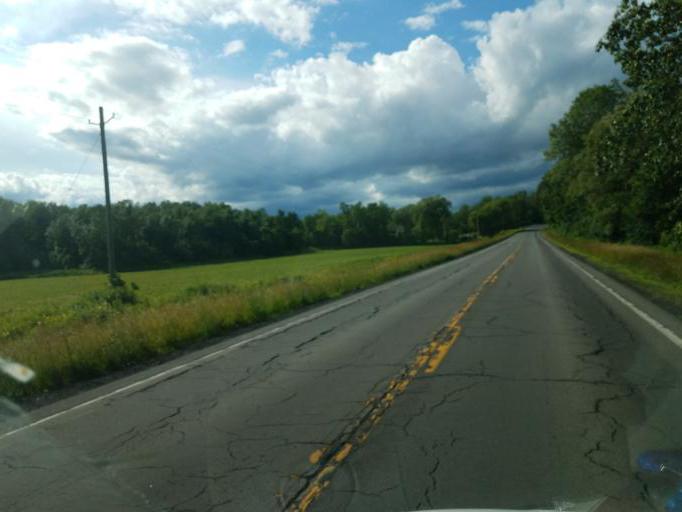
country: US
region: New York
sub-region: Wayne County
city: Clyde
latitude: 43.0430
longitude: -76.8635
